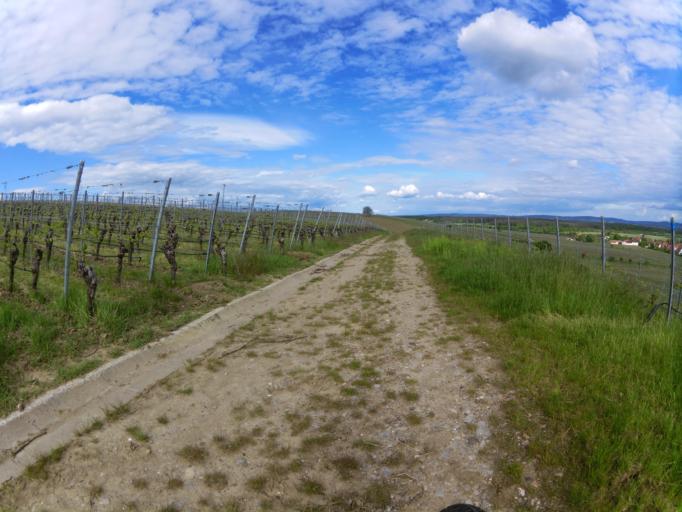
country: DE
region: Bavaria
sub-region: Regierungsbezirk Unterfranken
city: Sommerach
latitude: 49.8362
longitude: 10.2054
